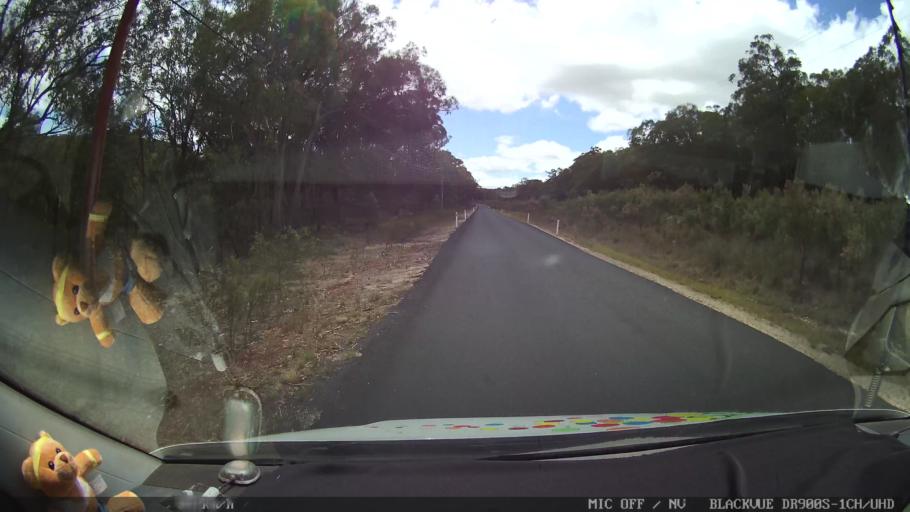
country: AU
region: New South Wales
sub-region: Glen Innes Severn
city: Glen Innes
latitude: -29.4391
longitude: 151.6237
